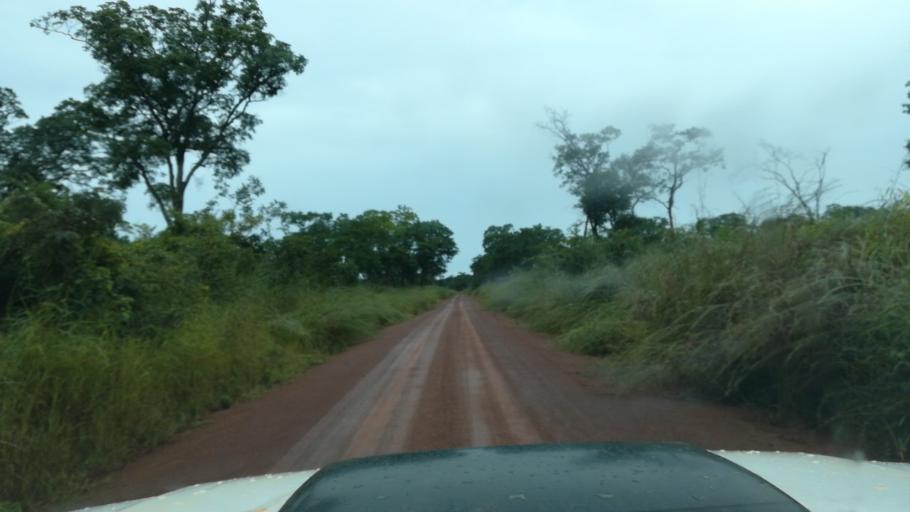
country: ZM
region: Luapula
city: Mwense
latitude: -10.3335
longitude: 28.1111
